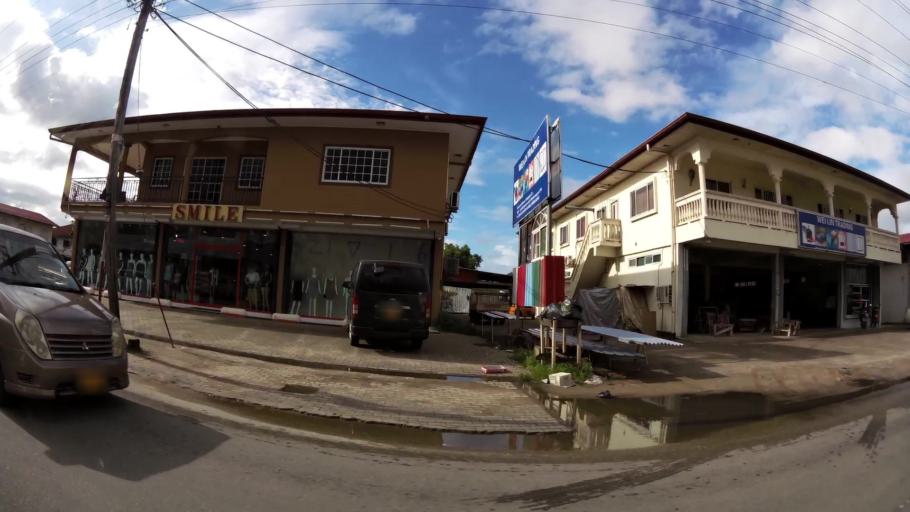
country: SR
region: Paramaribo
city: Paramaribo
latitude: 5.8446
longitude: -55.2201
